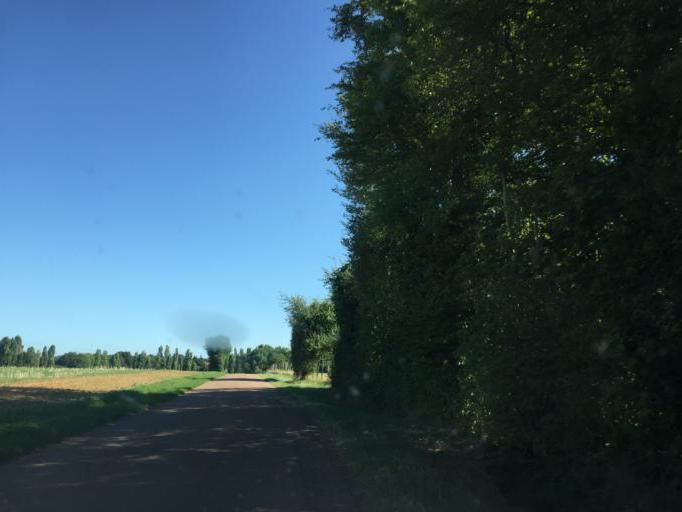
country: FR
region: Bourgogne
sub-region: Departement de l'Yonne
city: Fontenailles
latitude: 47.5094
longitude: 3.3444
